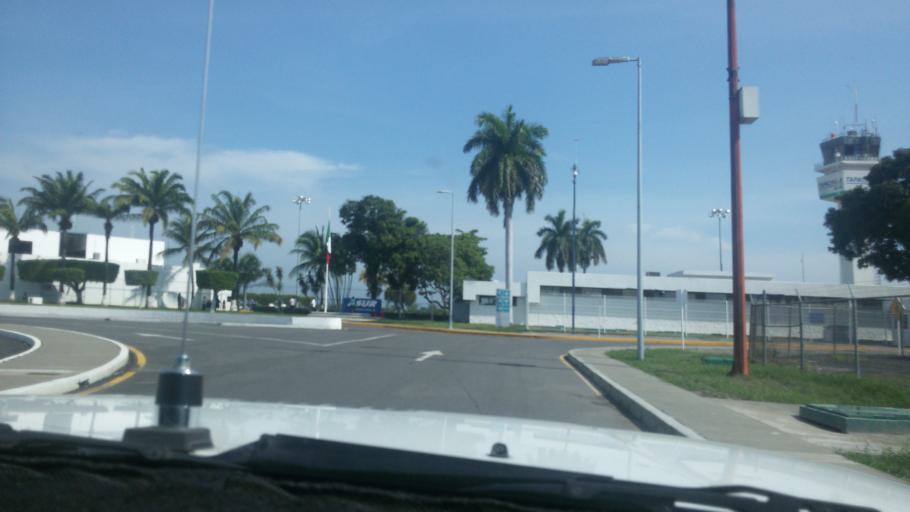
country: MX
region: Chiapas
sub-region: Tapachula
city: Congregacion Reforma
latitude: 14.7903
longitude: -92.3678
